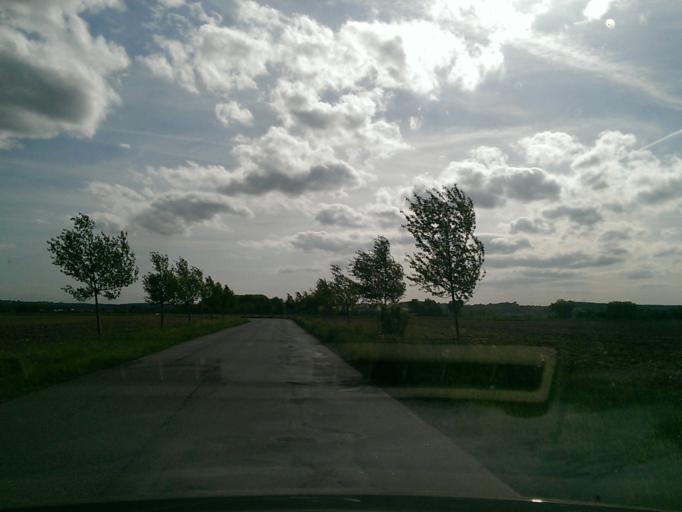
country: CZ
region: Central Bohemia
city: Bakov nad Jizerou
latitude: 50.4933
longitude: 14.9589
